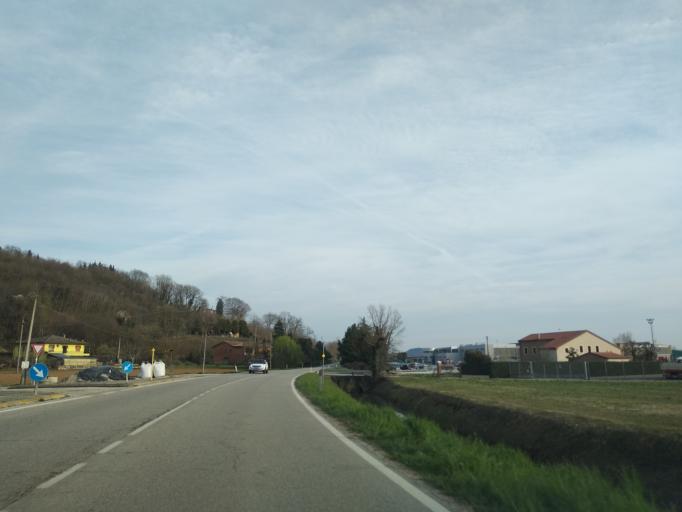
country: IT
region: Veneto
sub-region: Provincia di Vicenza
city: Ponte di Barbarano
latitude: 45.4002
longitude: 11.5618
